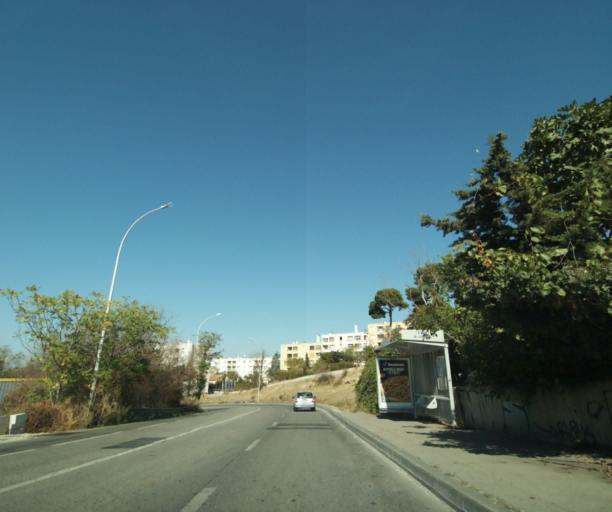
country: FR
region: Provence-Alpes-Cote d'Azur
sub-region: Departement des Bouches-du-Rhone
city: Marseille 14
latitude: 43.3375
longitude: 5.3851
